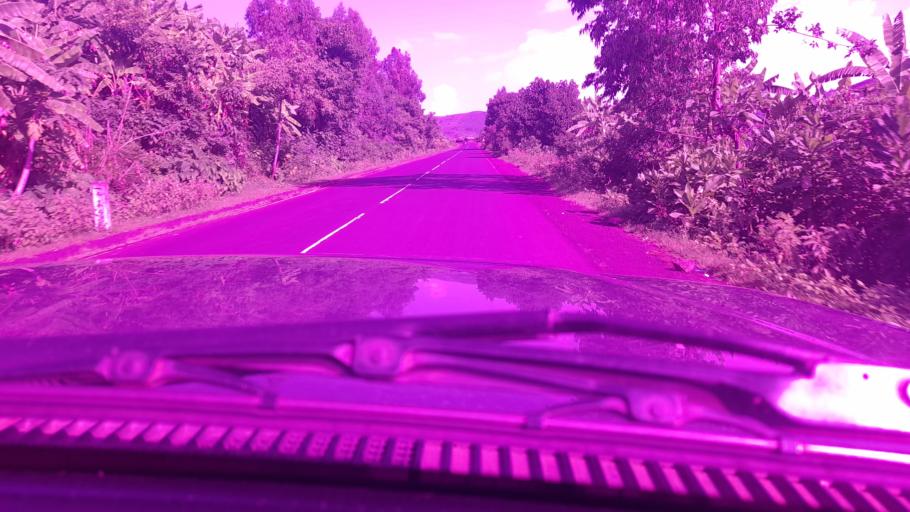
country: ET
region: Southern Nations, Nationalities, and People's Region
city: Bonga
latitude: 7.4842
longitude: 36.4596
